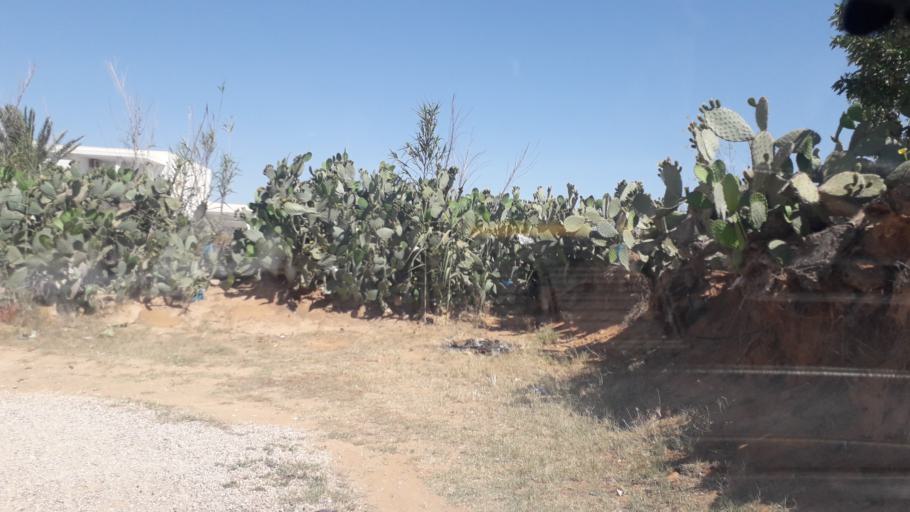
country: TN
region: Safaqis
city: Al Qarmadah
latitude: 34.8315
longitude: 10.7677
